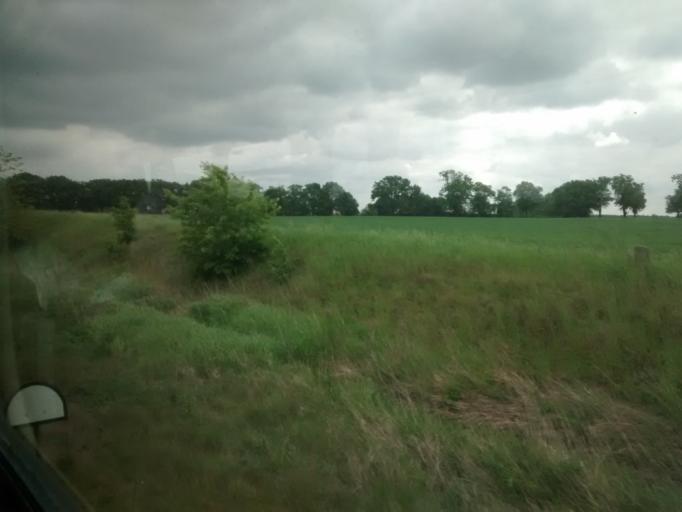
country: DE
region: Brandenburg
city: Glienicke
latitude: 52.6614
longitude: 13.3563
